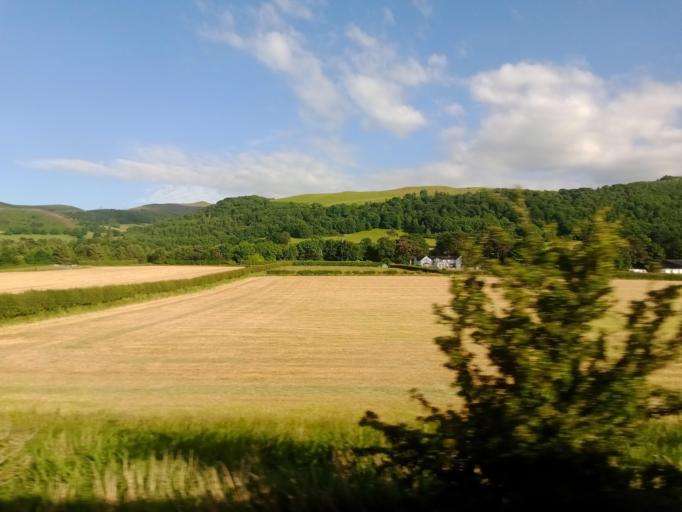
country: GB
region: Wales
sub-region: Gwynedd
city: Aber
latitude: 53.2449
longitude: -4.0045
